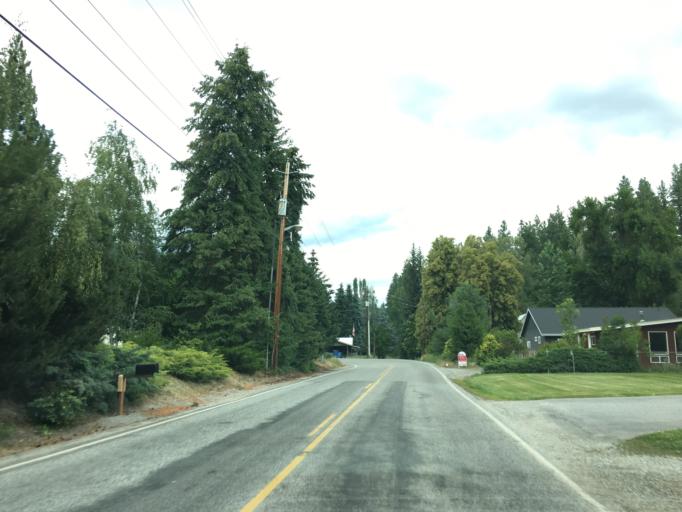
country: US
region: Washington
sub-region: Chelan County
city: Leavenworth
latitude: 47.5852
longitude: -120.6581
